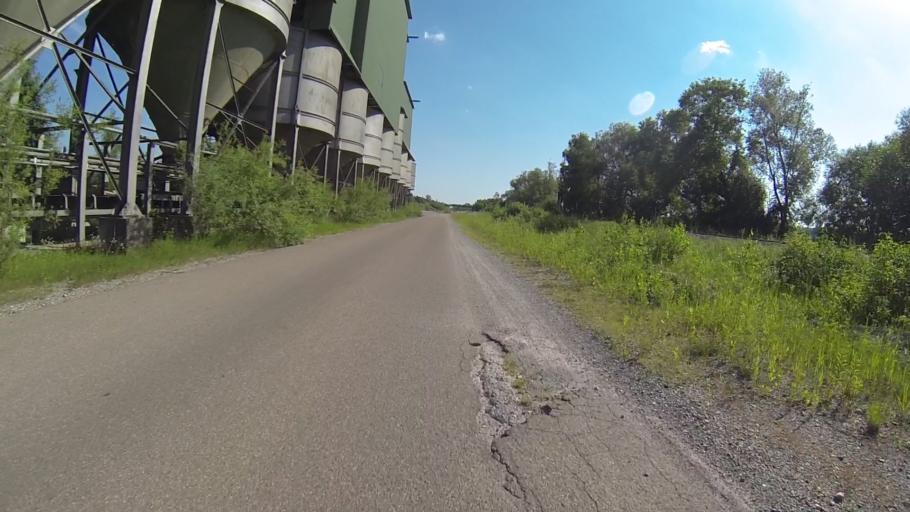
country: DE
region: Baden-Wuerttemberg
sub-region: Tuebingen Region
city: Laupheim
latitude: 48.2134
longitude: 9.8404
